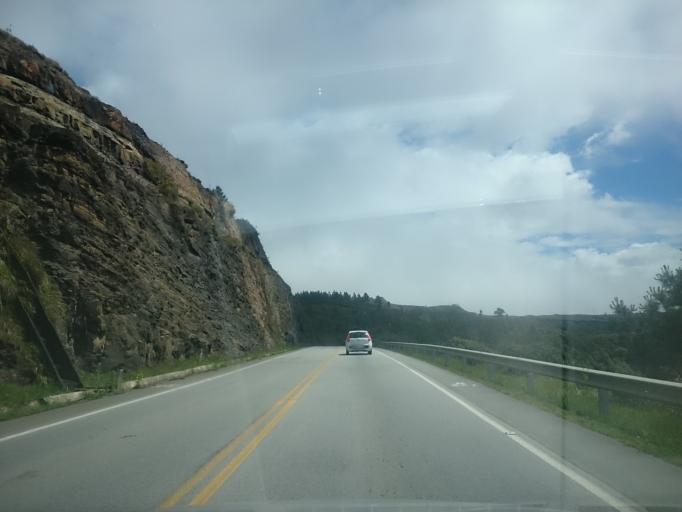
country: BR
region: Santa Catarina
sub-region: Anitapolis
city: Anitapolis
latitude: -27.6905
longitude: -49.1281
